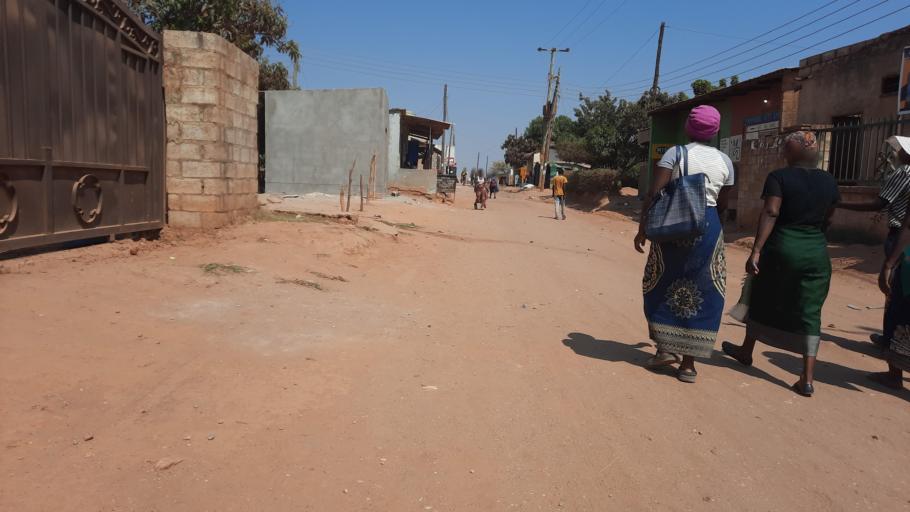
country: ZM
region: Lusaka
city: Lusaka
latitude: -15.3957
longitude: 28.3729
